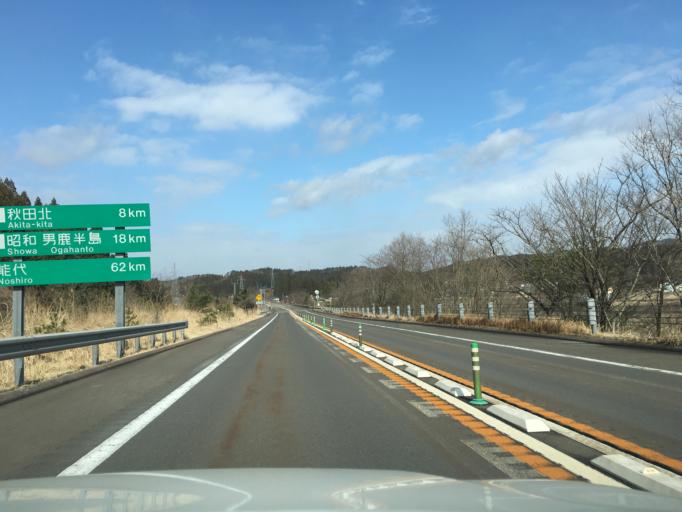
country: JP
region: Akita
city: Akita
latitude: 39.7345
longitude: 140.1757
